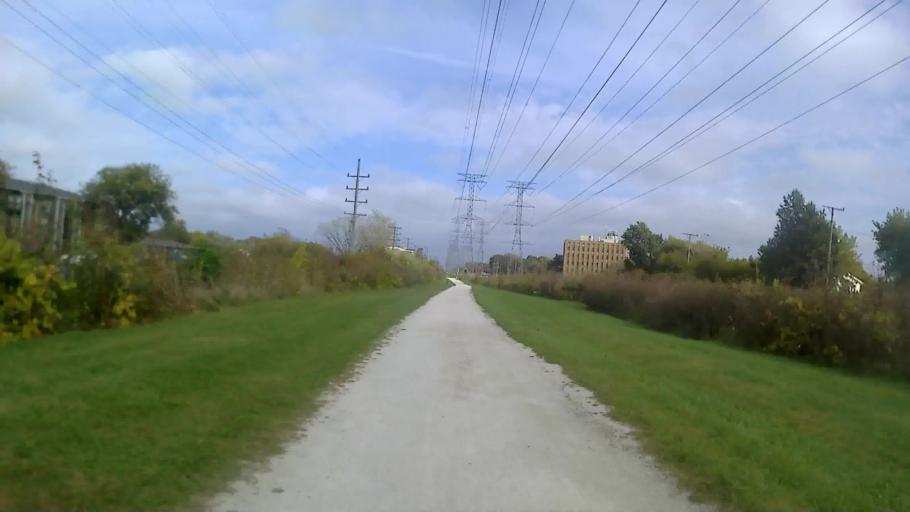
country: US
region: Illinois
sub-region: Kane County
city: Aurora
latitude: 41.7883
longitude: -88.2843
